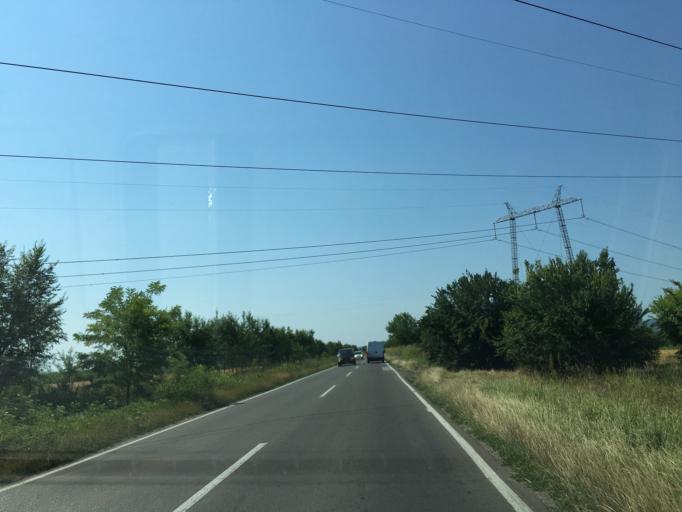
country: RS
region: Central Serbia
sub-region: Belgrade
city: Grocka
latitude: 44.7878
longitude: 20.7236
